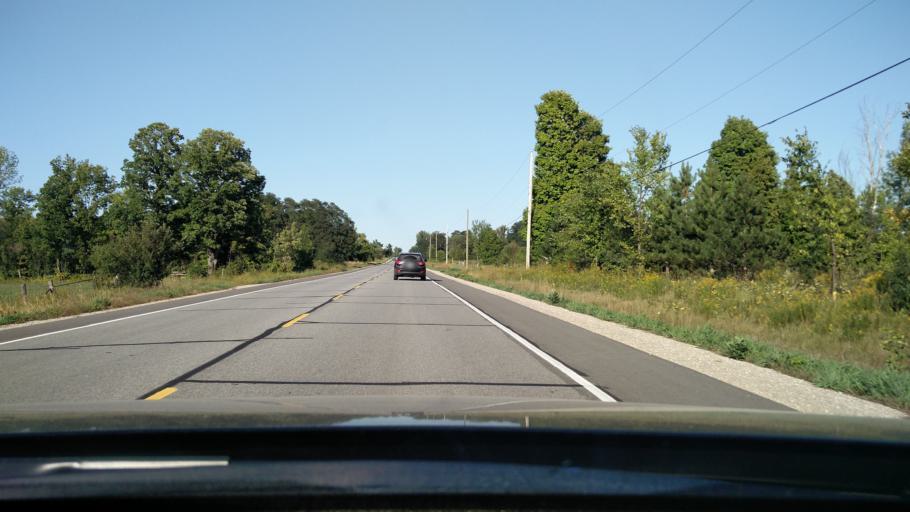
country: CA
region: Ontario
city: Perth
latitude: 44.9612
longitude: -76.1523
